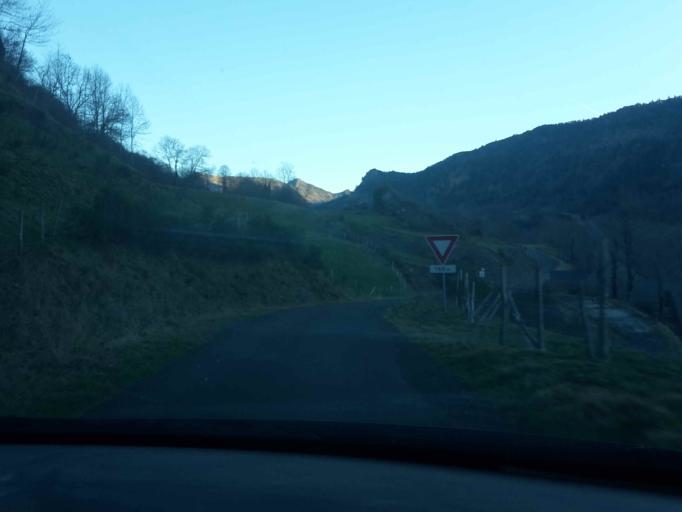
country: FR
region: Auvergne
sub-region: Departement du Cantal
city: Riom-es-Montagnes
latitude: 45.1632
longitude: 2.6109
